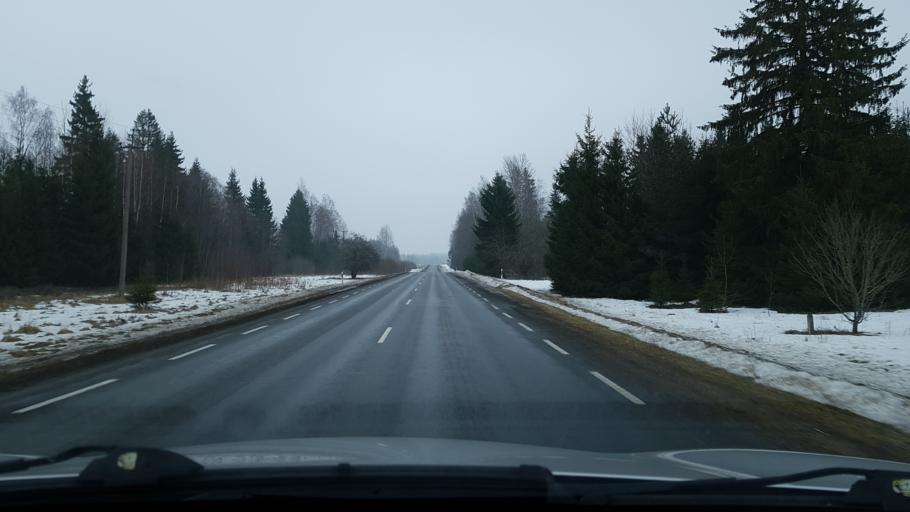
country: EE
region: Viljandimaa
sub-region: Viiratsi vald
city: Viiratsi
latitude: 58.2502
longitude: 25.7595
